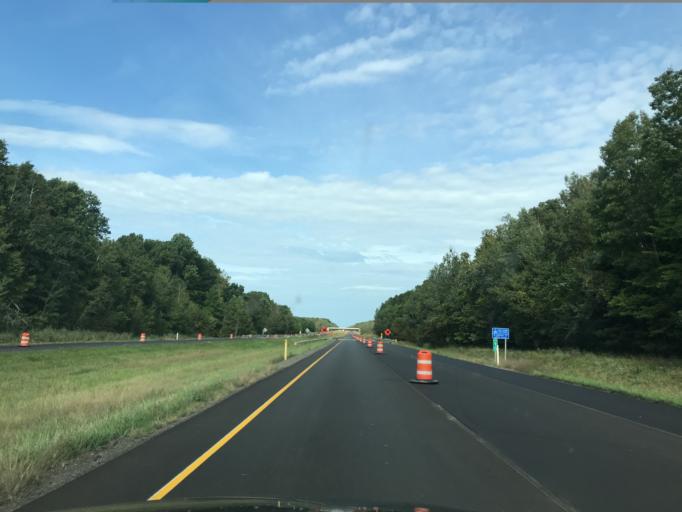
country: US
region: Ohio
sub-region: Ashtabula County
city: Jefferson
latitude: 41.7767
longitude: -80.7290
